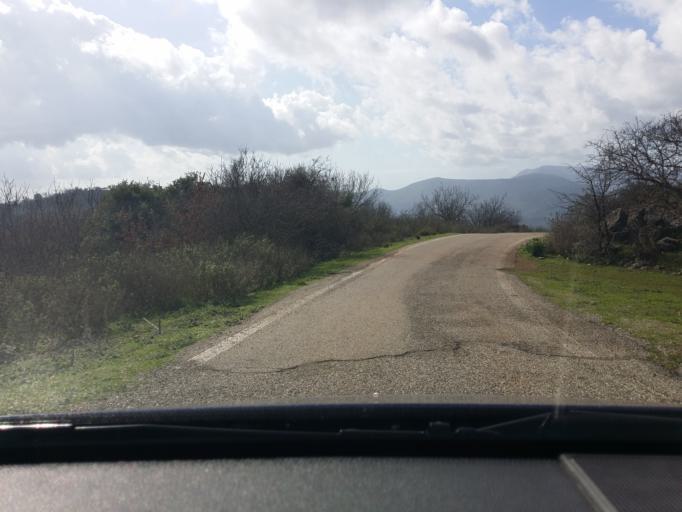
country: GR
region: West Greece
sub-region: Nomos Aitolias kai Akarnanias
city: Fitiai
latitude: 38.6455
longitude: 21.1969
